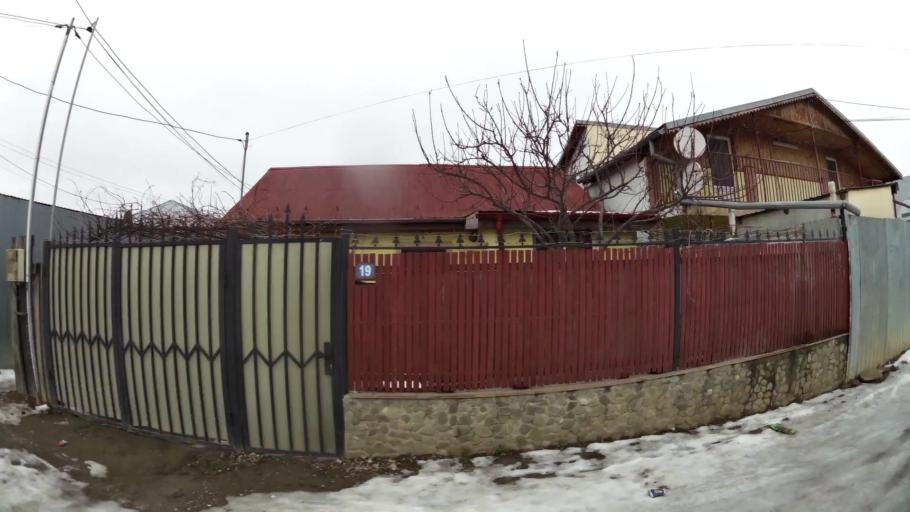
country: RO
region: Ilfov
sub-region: Comuna Pantelimon
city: Pantelimon
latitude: 44.4567
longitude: 26.1979
